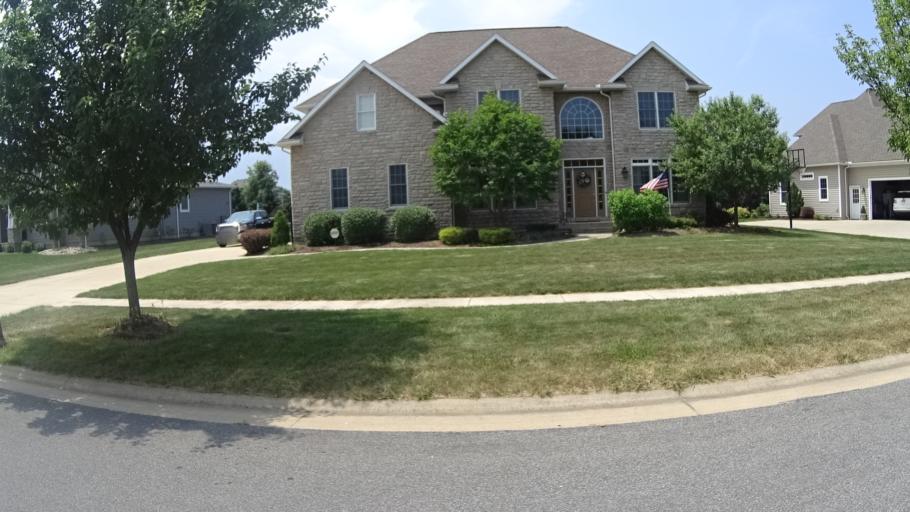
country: US
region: Ohio
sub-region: Erie County
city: Huron
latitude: 41.3842
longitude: -82.5307
